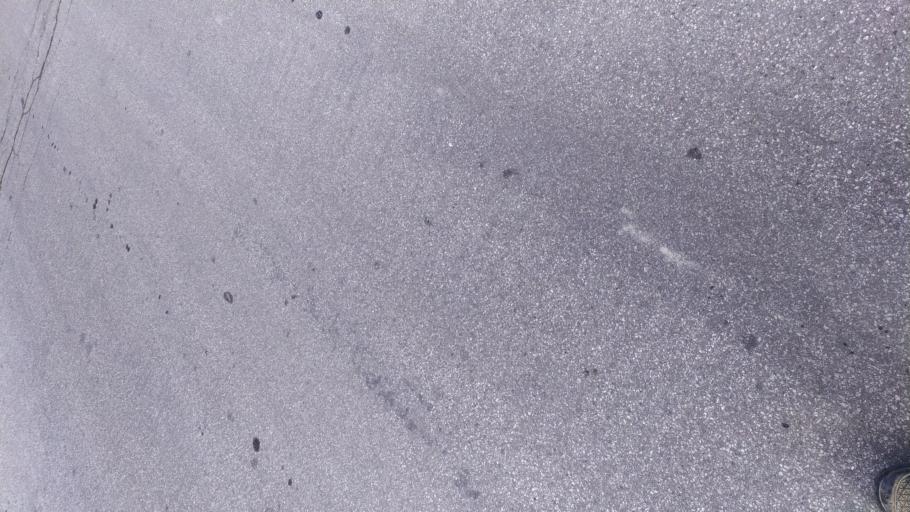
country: IT
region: Sicily
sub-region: Messina
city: San Pier Niceto
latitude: 38.1606
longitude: 15.3496
